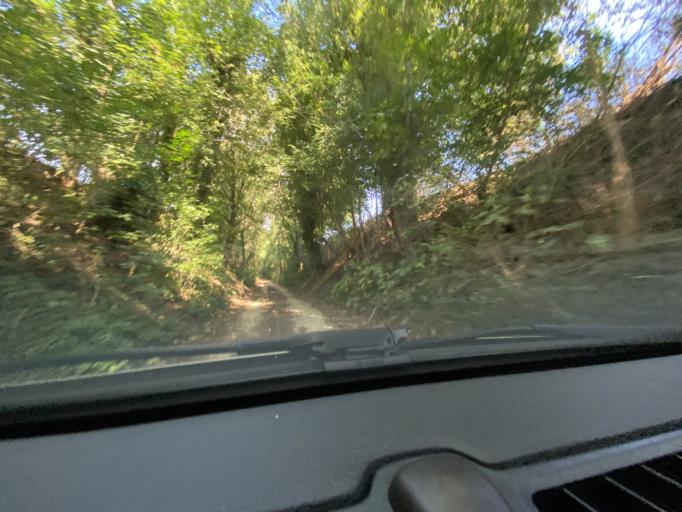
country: NL
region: Limburg
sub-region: Gemeente Nuth
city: Nuth
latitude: 50.9163
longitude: 5.8643
